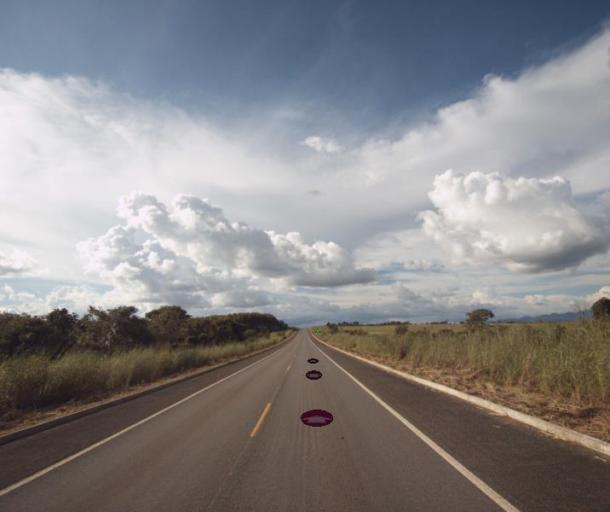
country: BR
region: Goias
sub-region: Barro Alto
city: Barro Alto
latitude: -14.8321
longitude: -48.6383
